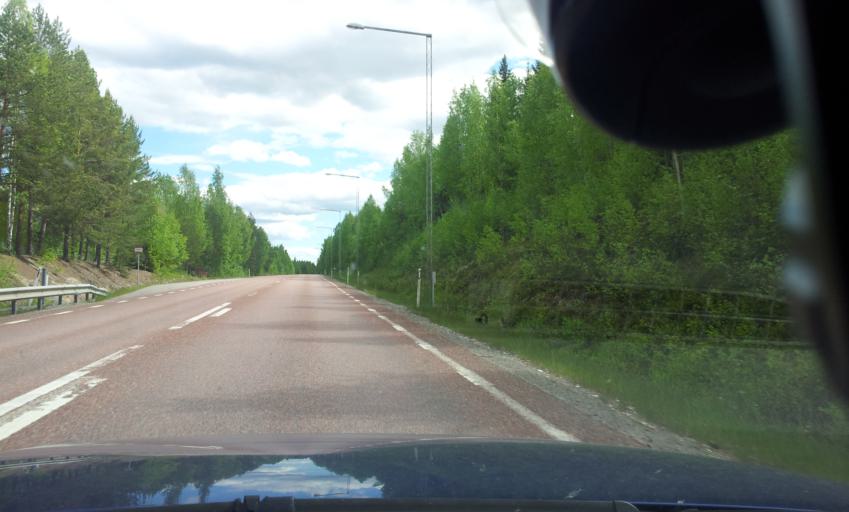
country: SE
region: Gaevleborg
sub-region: Bollnas Kommun
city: Arbra
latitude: 61.5732
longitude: 16.3208
